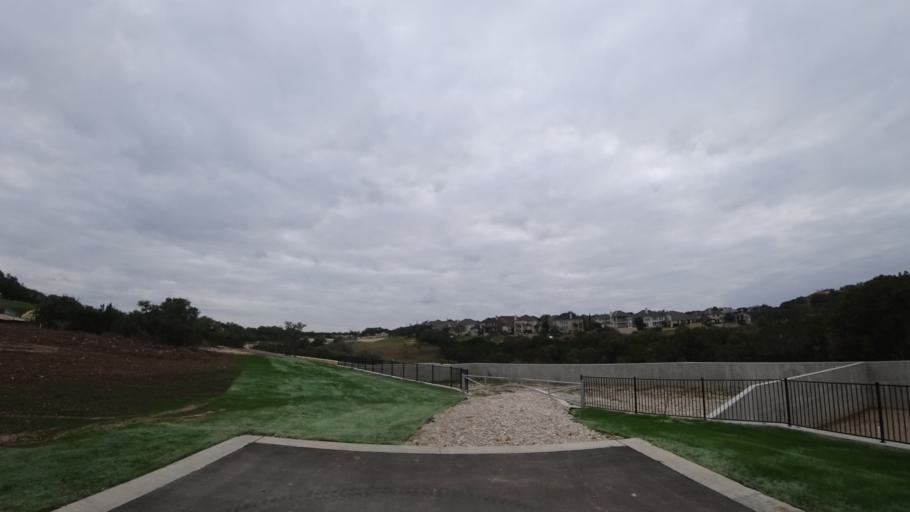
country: US
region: Texas
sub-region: Travis County
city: Bee Cave
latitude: 30.3181
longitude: -97.9134
